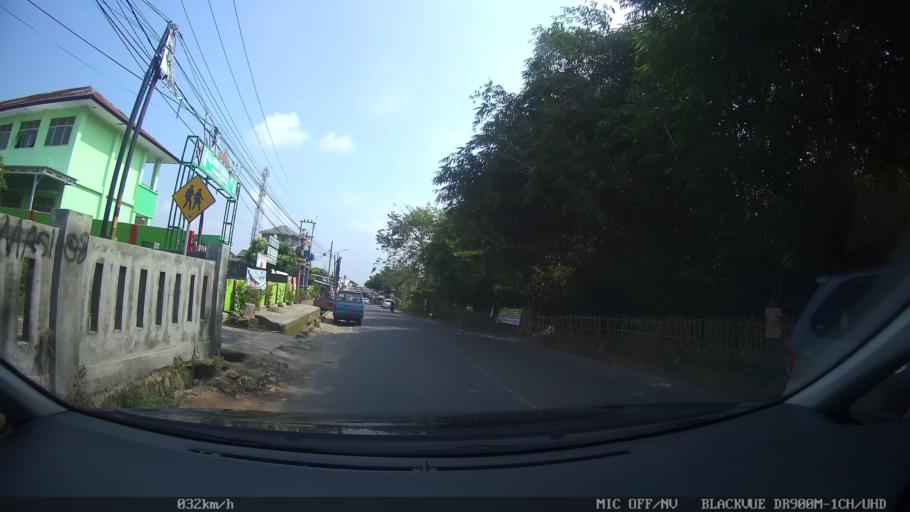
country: ID
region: Lampung
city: Kedaton
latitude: -5.3533
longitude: 105.2634
